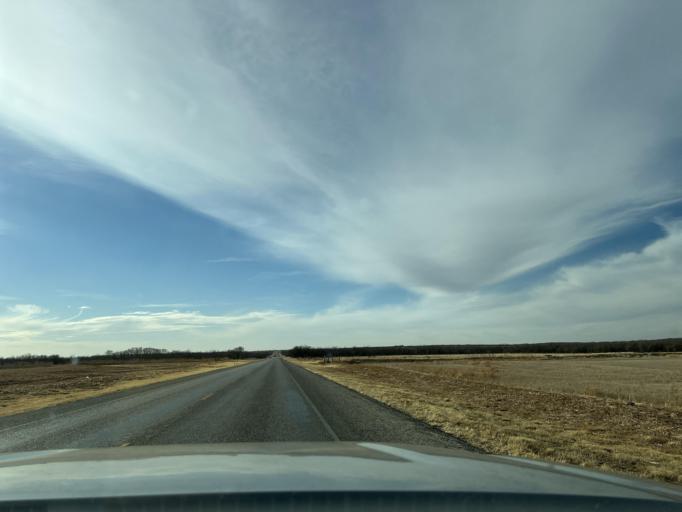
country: US
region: Texas
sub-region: Fisher County
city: Rotan
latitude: 32.7401
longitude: -100.5059
